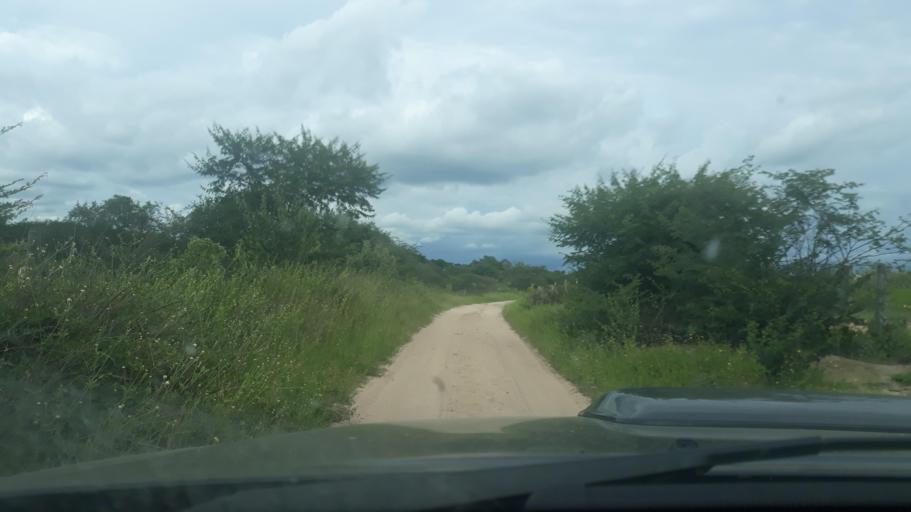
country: BR
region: Bahia
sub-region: Riacho De Santana
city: Riacho de Santana
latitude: -13.8548
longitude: -43.0579
